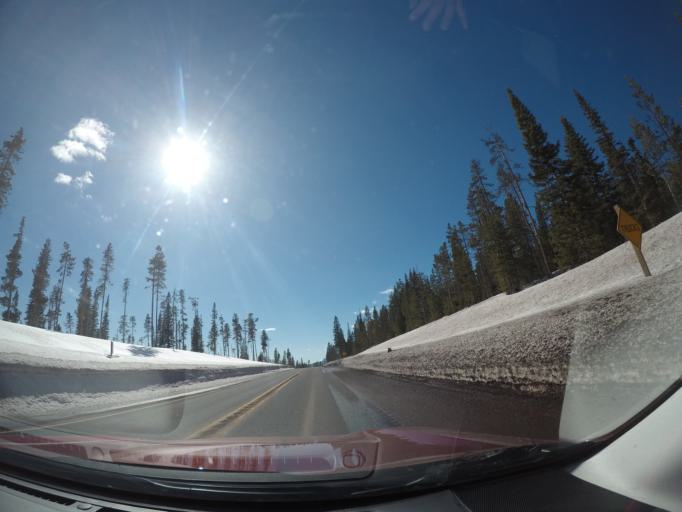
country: US
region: Oregon
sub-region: Deschutes County
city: Sunriver
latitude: 43.9835
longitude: -121.5802
